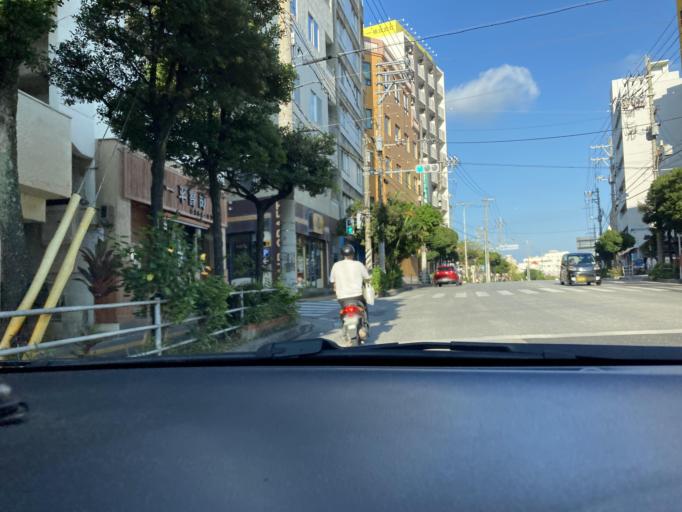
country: JP
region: Okinawa
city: Naha-shi
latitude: 26.2051
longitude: 127.6987
